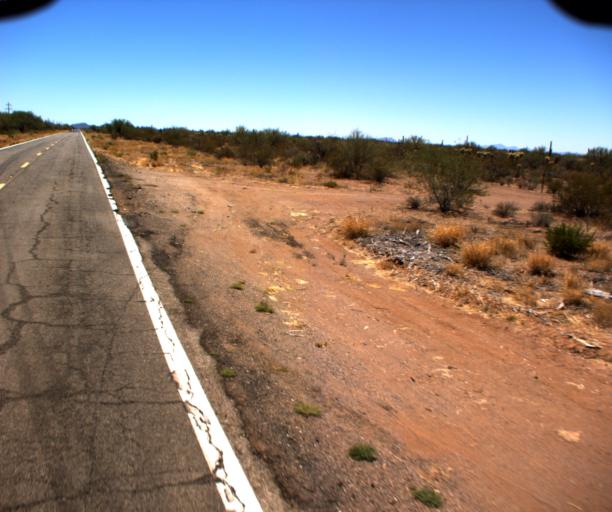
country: US
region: Arizona
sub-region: Pima County
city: Sells
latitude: 32.0698
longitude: -112.0412
